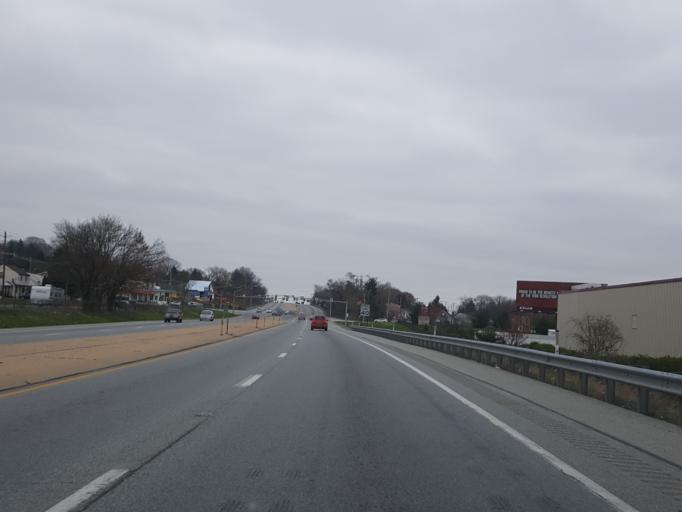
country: US
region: Pennsylvania
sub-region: York County
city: North York
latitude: 39.9823
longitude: -76.7119
